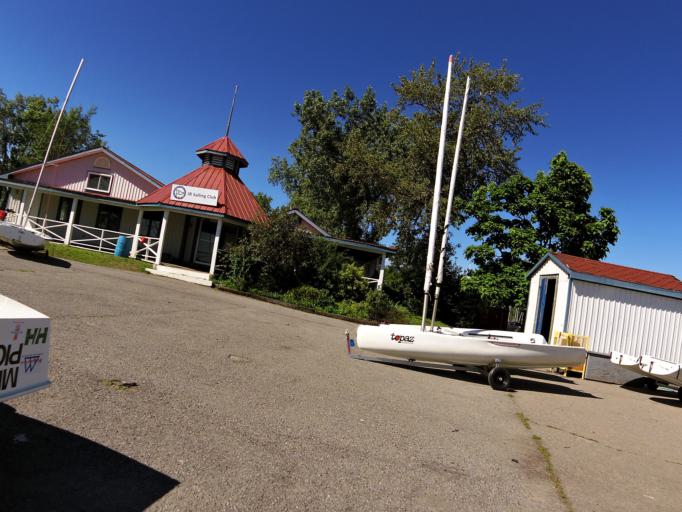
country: CA
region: Ontario
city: Bells Corners
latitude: 45.3726
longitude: -75.8034
